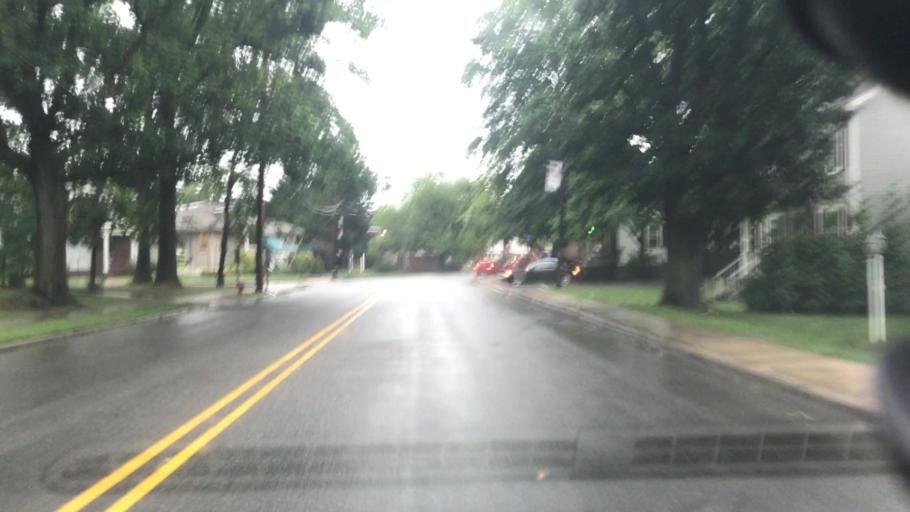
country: US
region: New Jersey
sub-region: Union County
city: Clark
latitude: 40.6221
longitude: -74.3063
